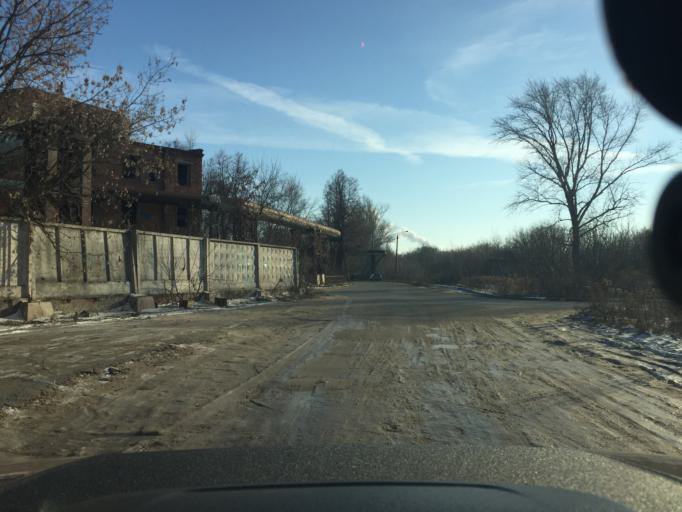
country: RU
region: Tula
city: Tula
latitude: 54.1762
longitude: 37.7015
